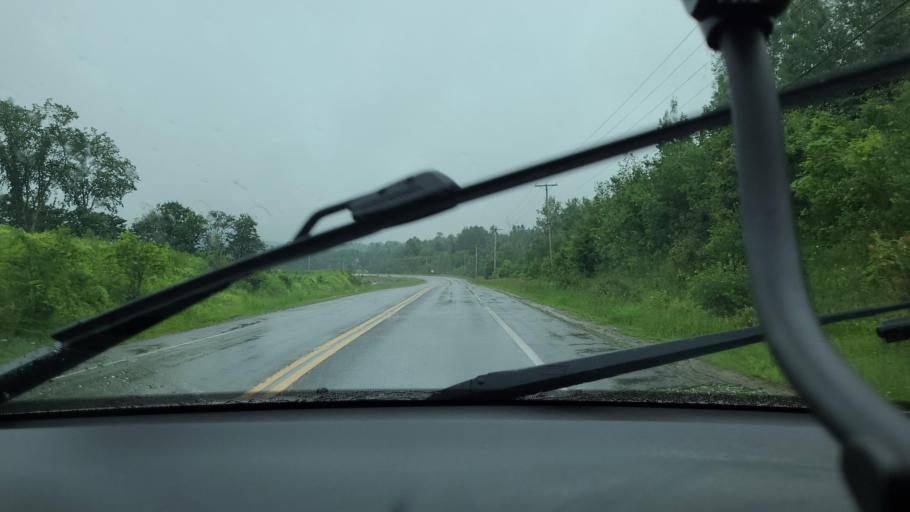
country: CA
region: Quebec
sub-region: Outaouais
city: Saint-Andre-Avellin
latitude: 45.6782
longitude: -75.0397
